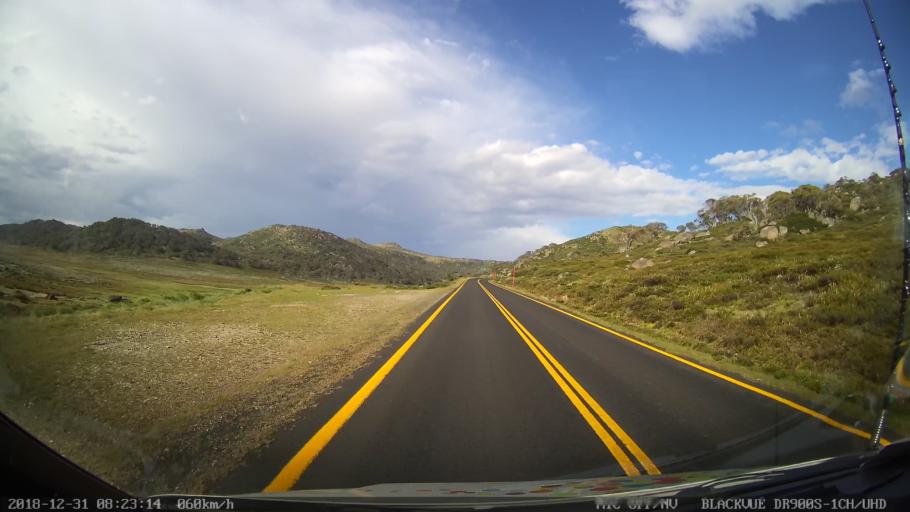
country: AU
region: New South Wales
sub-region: Snowy River
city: Jindabyne
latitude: -36.4275
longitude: 148.3510
